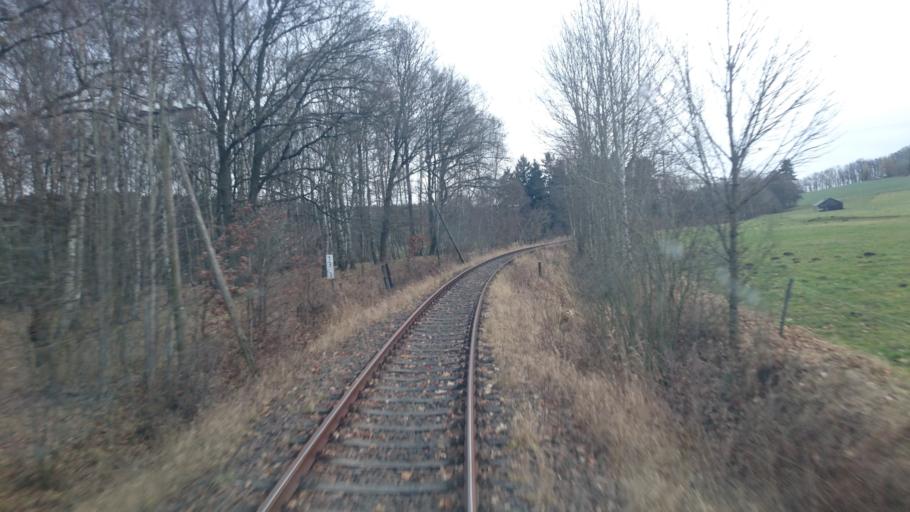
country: DE
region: Thuringia
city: Oettersdorf
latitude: 50.5853
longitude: 11.8380
